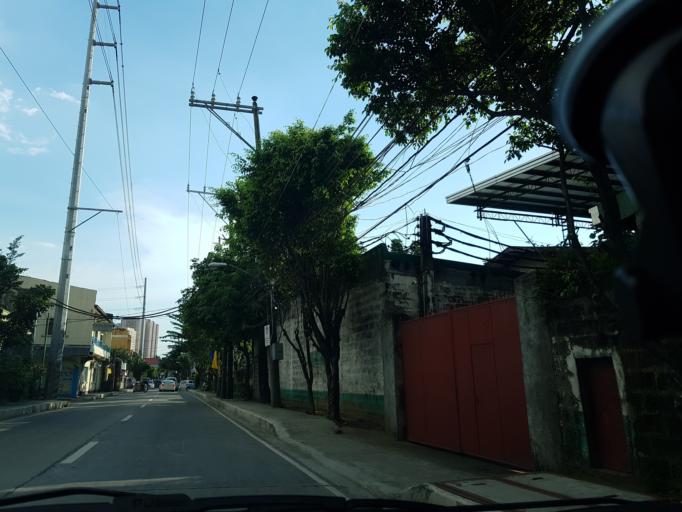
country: PH
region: Metro Manila
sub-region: Marikina
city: Calumpang
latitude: 14.6201
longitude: 121.0826
